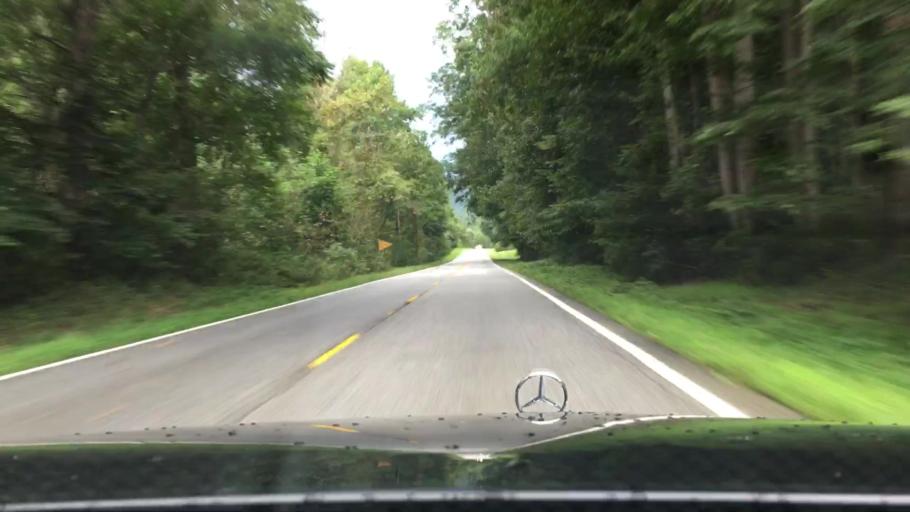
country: US
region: Virginia
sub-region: Nelson County
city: Nellysford
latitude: 37.8245
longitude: -78.9355
